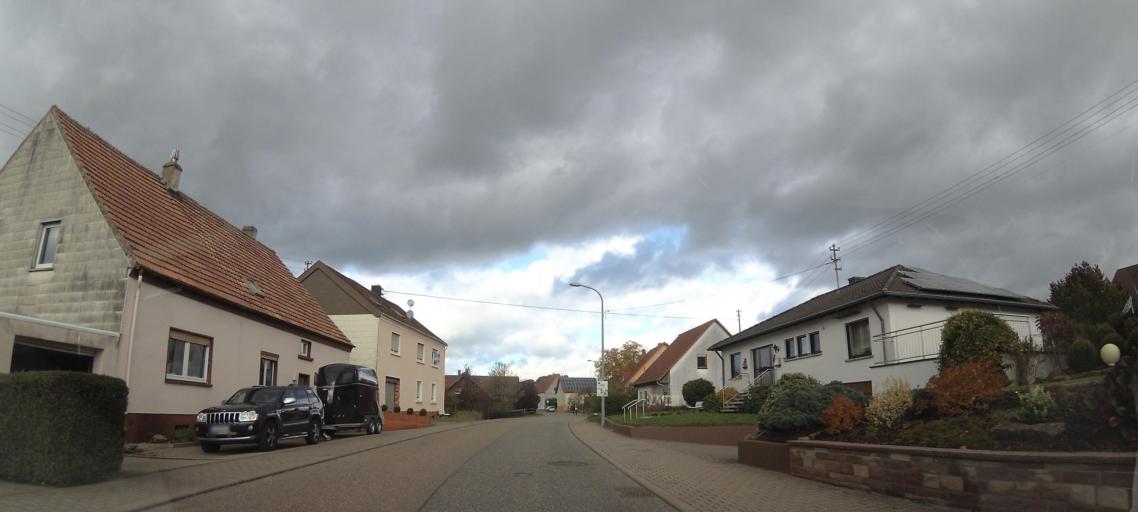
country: DE
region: Rheinland-Pfalz
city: Dietrichingen
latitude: 49.1866
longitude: 7.4135
